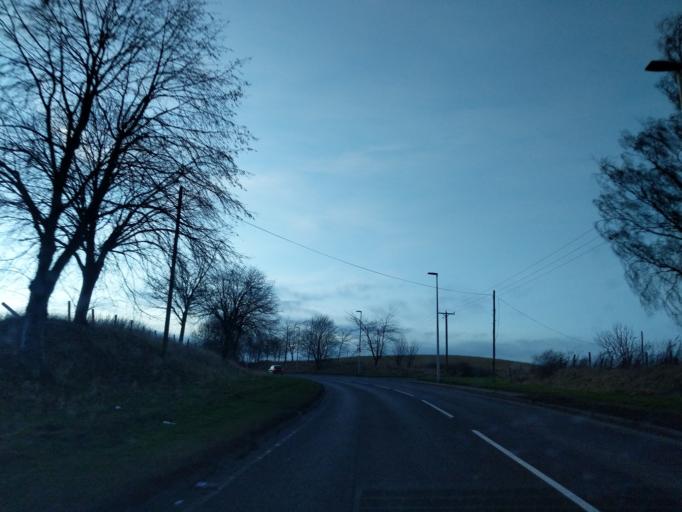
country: GB
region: Scotland
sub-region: Midlothian
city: Bonnyrigg
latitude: 55.8812
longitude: -3.1294
